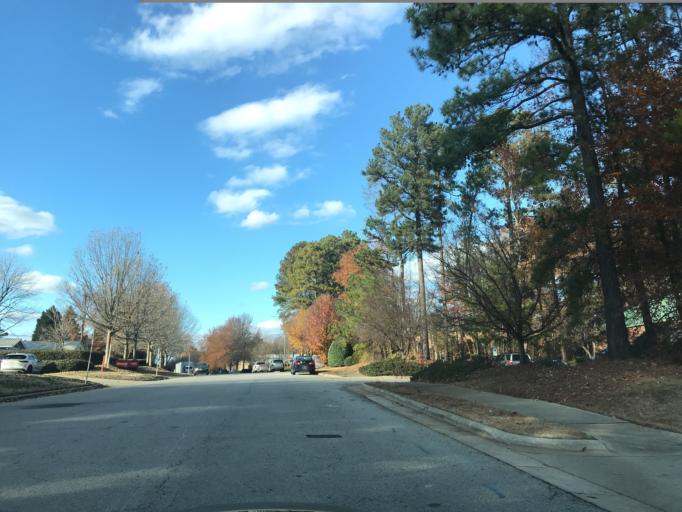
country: US
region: North Carolina
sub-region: Wake County
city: Raleigh
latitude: 35.8491
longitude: -78.5904
